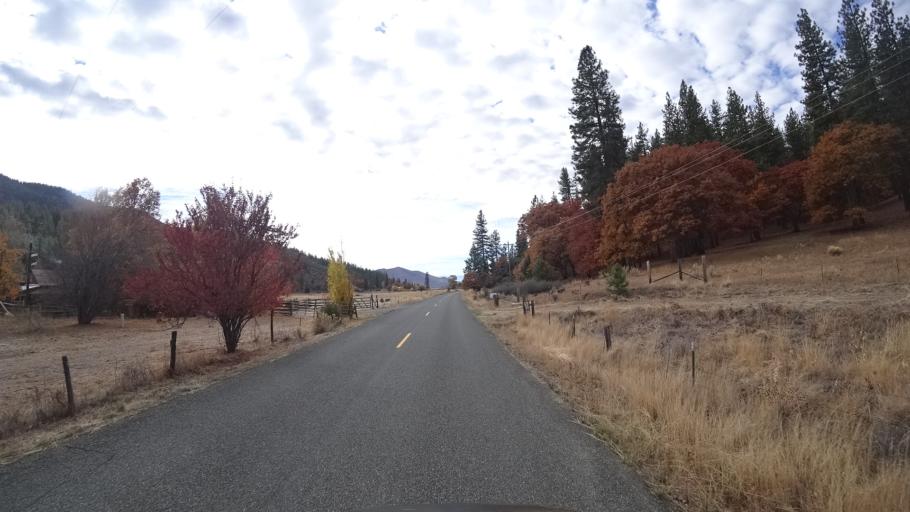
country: US
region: California
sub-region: Siskiyou County
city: Yreka
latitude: 41.6681
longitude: -122.8337
